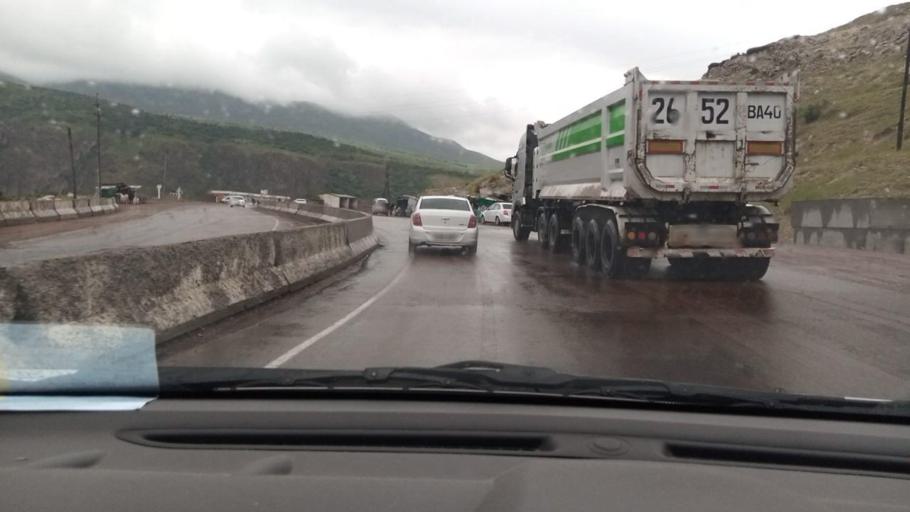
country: UZ
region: Toshkent
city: Angren
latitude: 41.0740
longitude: 70.2514
